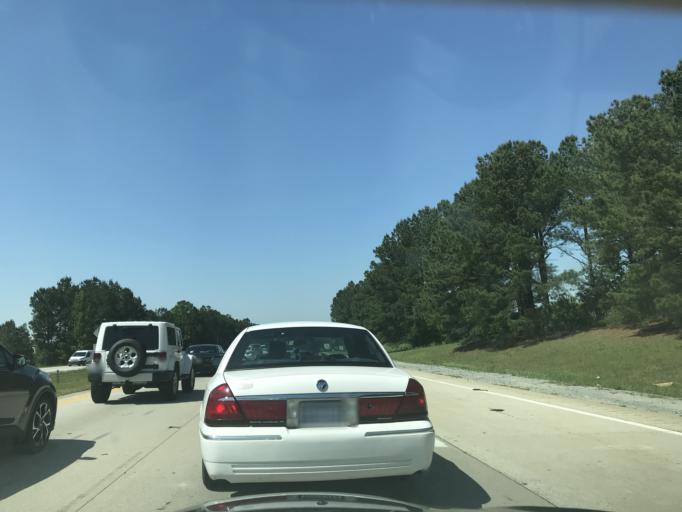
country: US
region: North Carolina
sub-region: Wake County
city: Garner
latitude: 35.6125
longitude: -78.5665
